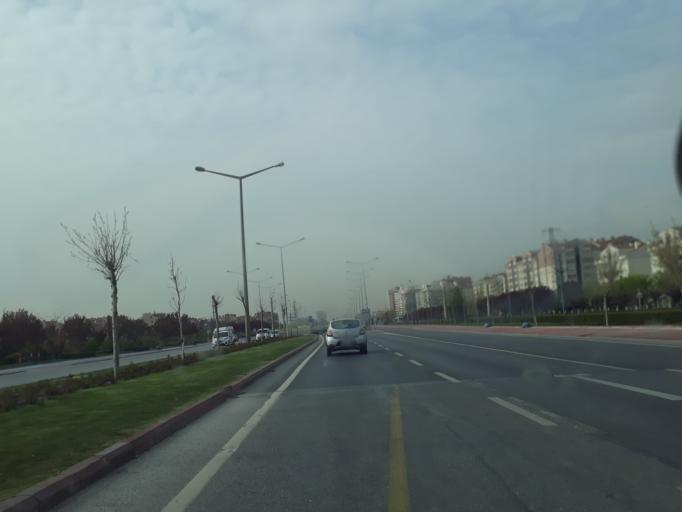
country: TR
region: Konya
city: Selcuklu
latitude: 37.9625
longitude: 32.5146
